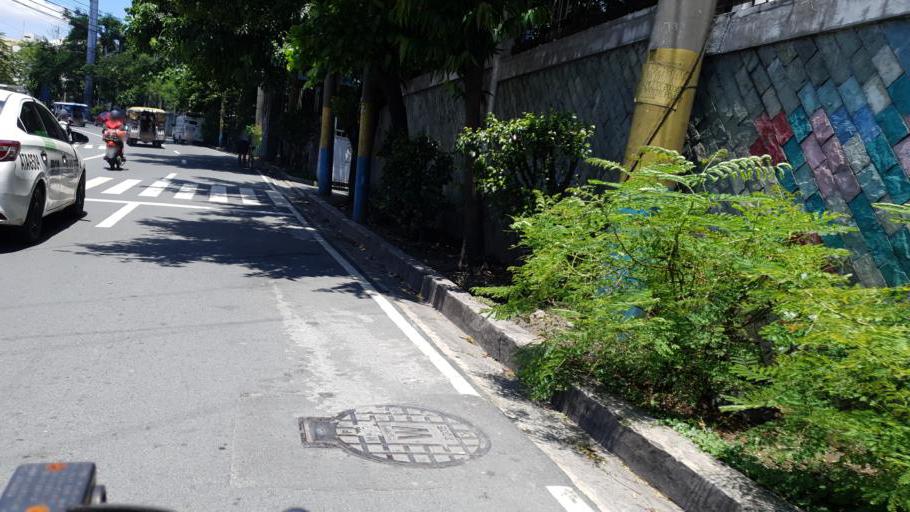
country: PH
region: Calabarzon
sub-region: Province of Rizal
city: Pateros
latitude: 14.5575
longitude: 121.0659
